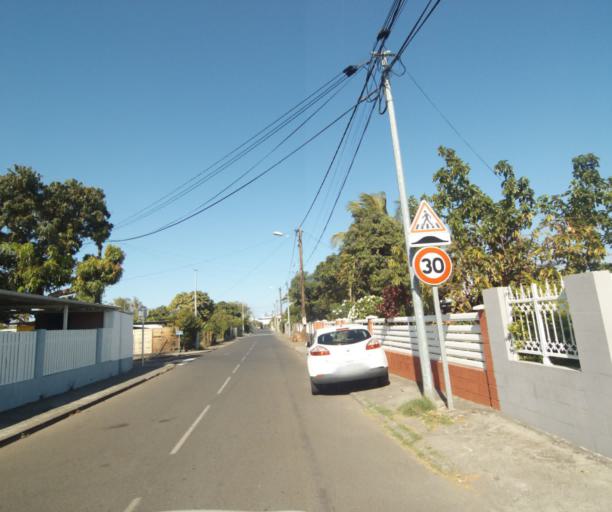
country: RE
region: Reunion
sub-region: Reunion
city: Saint-Paul
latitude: -20.9851
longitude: 55.2951
